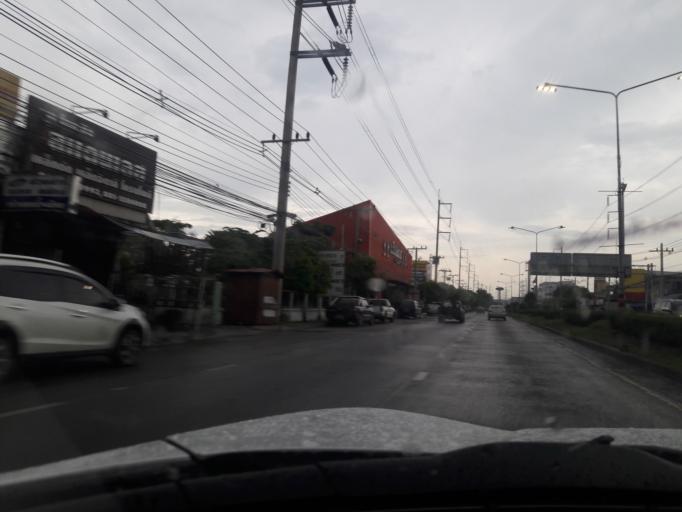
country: TH
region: Lop Buri
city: Lop Buri
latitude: 14.7995
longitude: 100.6561
